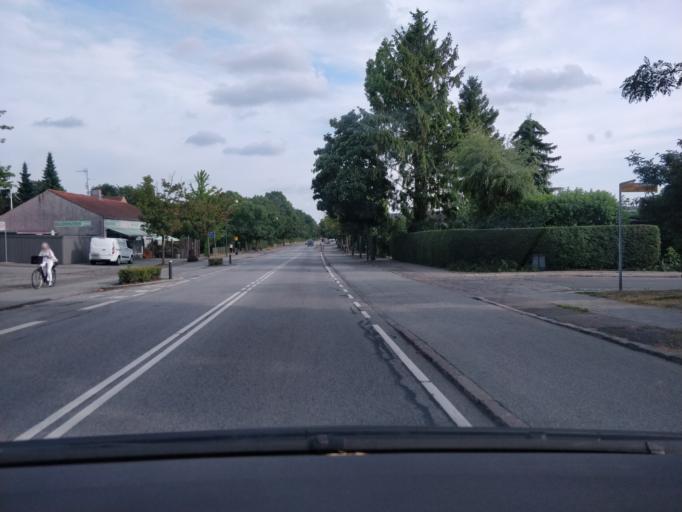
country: DK
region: Capital Region
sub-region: Herlev Kommune
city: Herlev
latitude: 55.7352
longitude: 12.4337
